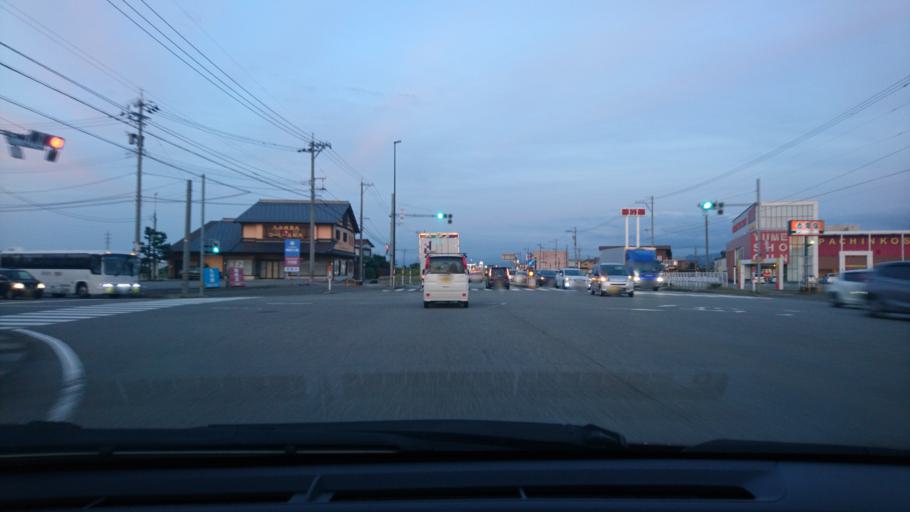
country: JP
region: Ishikawa
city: Komatsu
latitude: 36.3050
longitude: 136.3481
